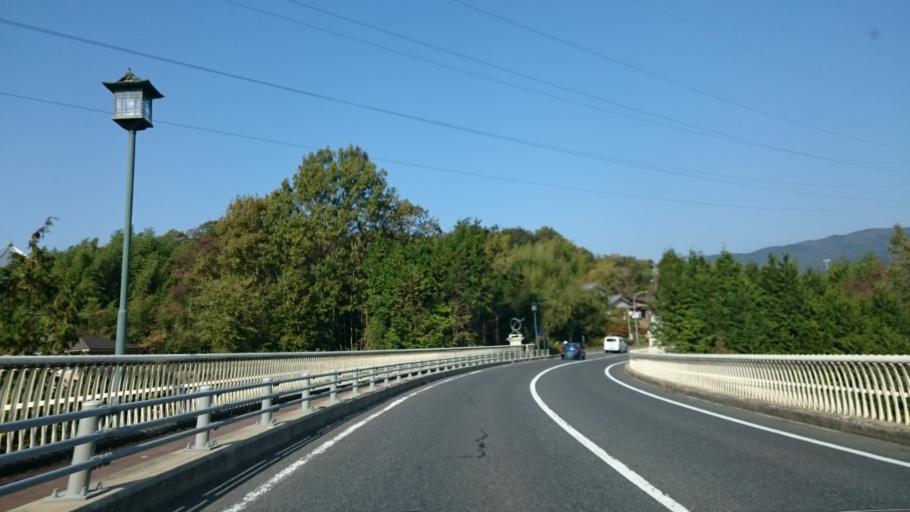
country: JP
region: Gifu
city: Nakatsugawa
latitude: 35.5105
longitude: 137.4742
